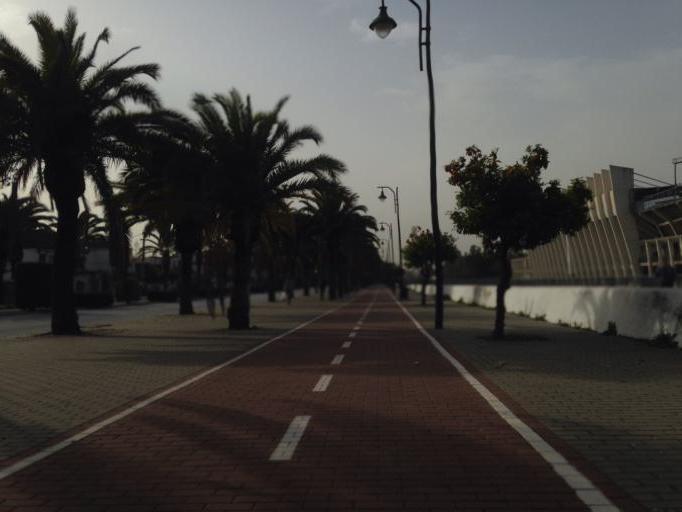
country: ES
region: Andalusia
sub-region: Provincia de Malaga
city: Malaga
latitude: 36.7361
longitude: -4.4250
